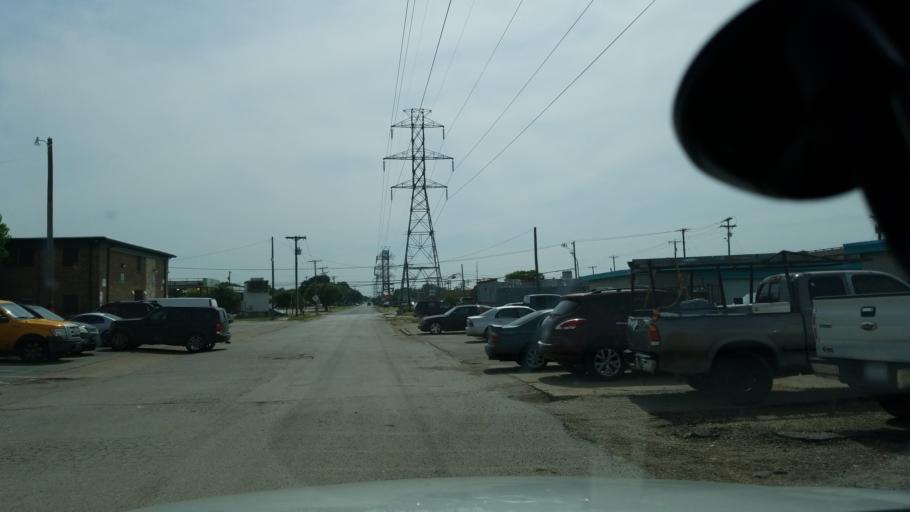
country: US
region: Texas
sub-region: Dallas County
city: Irving
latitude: 32.8162
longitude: -96.9777
